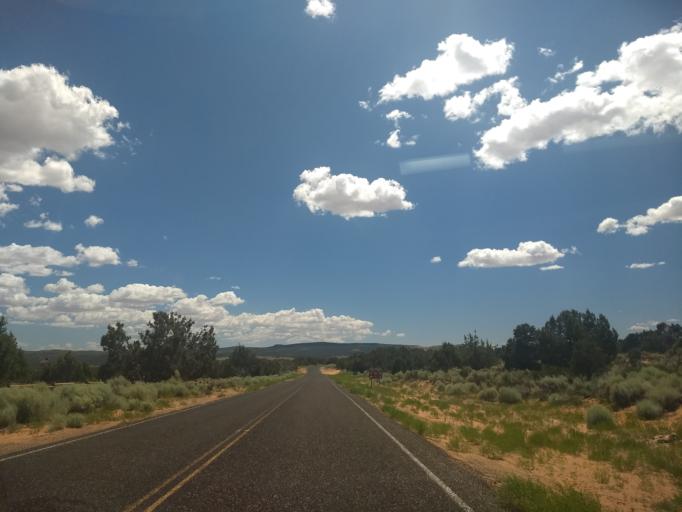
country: US
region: Utah
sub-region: Kane County
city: Kanab
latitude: 37.0389
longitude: -112.7307
